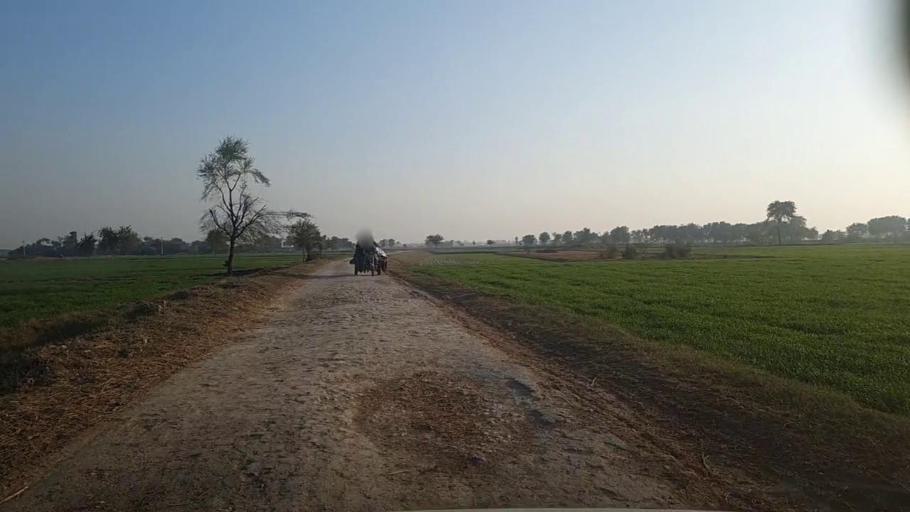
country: PK
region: Sindh
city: Khairpur
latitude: 28.0720
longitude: 69.7497
